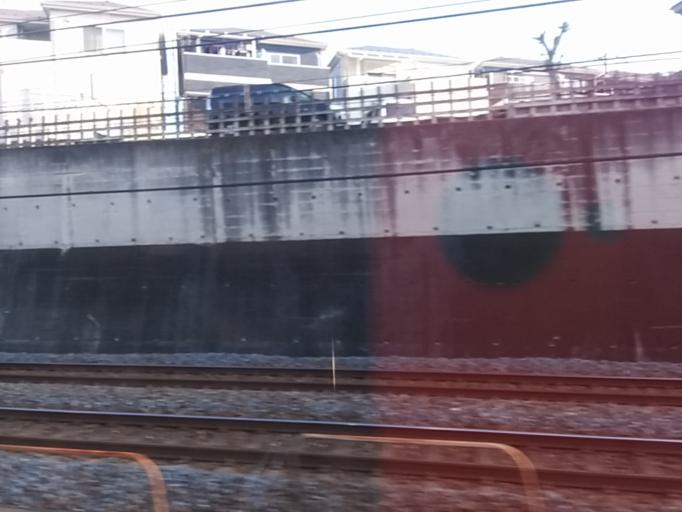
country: JP
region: Saitama
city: Asaka
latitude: 35.8081
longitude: 139.5956
